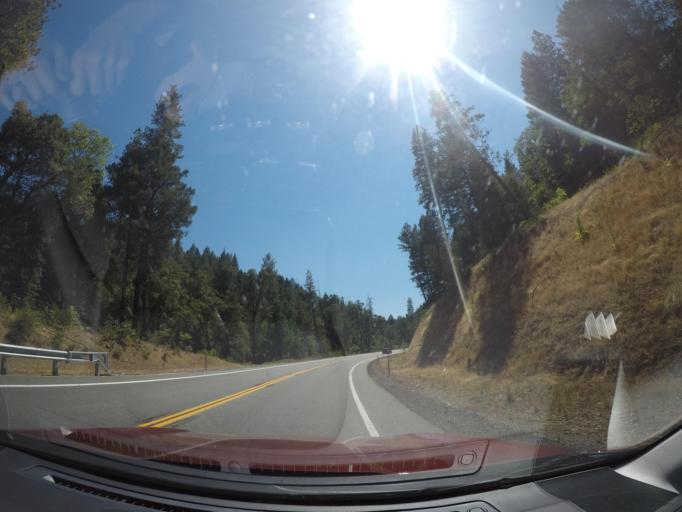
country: US
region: California
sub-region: Shasta County
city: Bella Vista
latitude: 40.7613
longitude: -122.0127
